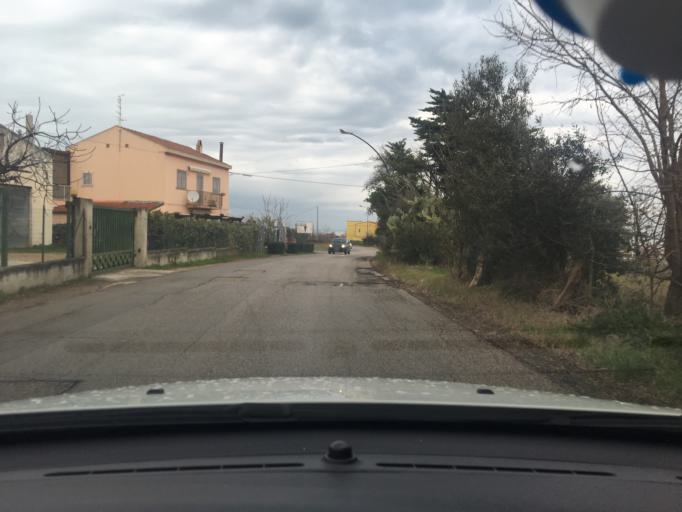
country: IT
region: Molise
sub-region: Provincia di Campobasso
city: Termoli
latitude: 41.9791
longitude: 14.9994
